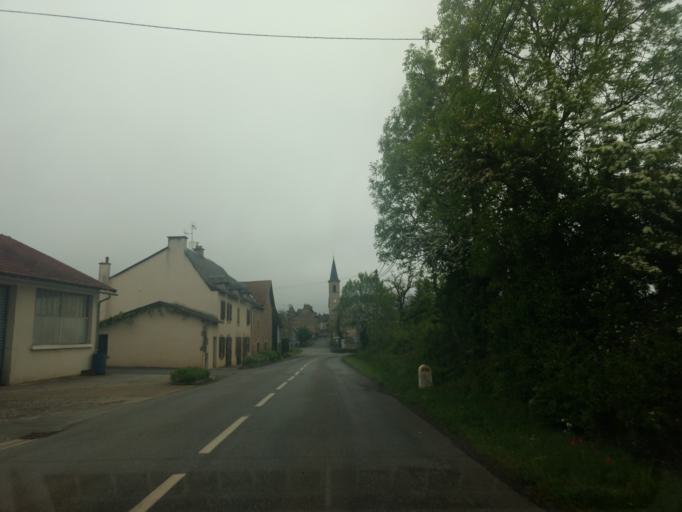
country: FR
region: Midi-Pyrenees
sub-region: Departement de l'Aveyron
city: Montbazens
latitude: 44.4515
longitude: 2.2527
